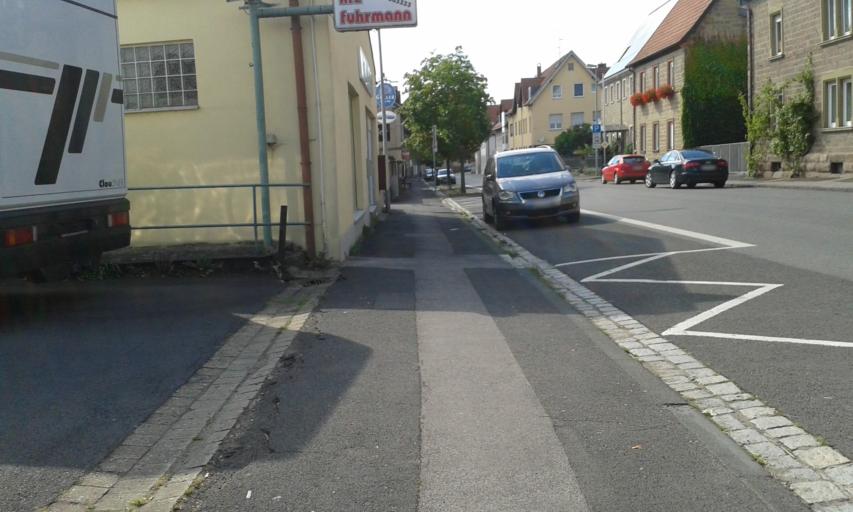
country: DE
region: Bavaria
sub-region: Regierungsbezirk Unterfranken
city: Zeil
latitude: 50.0069
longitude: 10.5988
